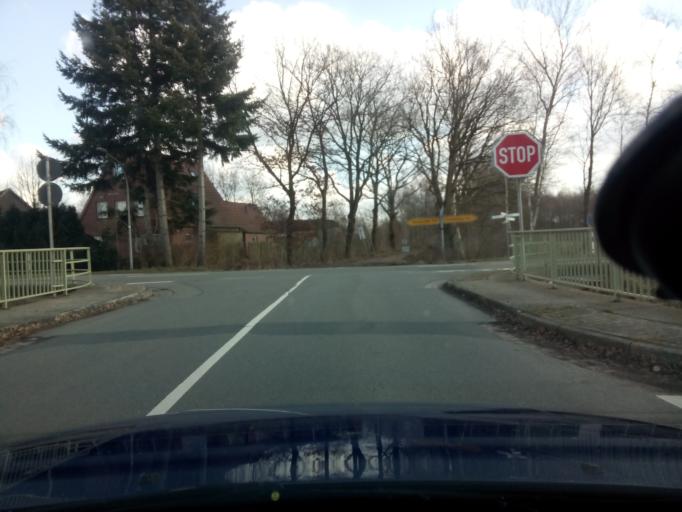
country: DE
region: Lower Saxony
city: Basdahl
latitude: 53.4149
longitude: 9.0460
